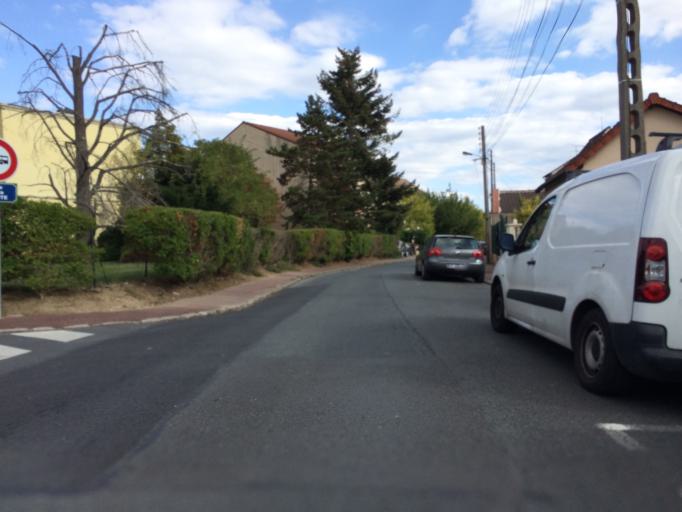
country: FR
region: Ile-de-France
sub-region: Departement de l'Essonne
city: Chilly-Mazarin
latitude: 48.7069
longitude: 2.3239
